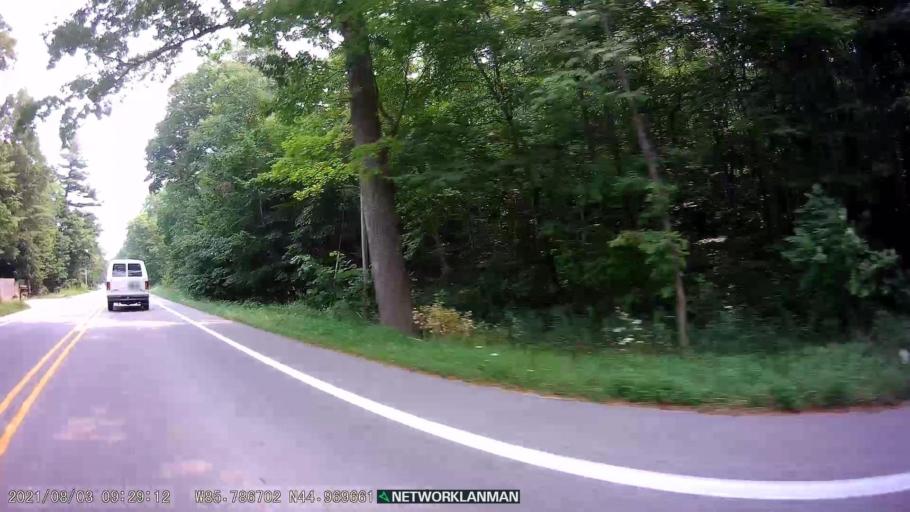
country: US
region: Michigan
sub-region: Leelanau County
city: Leland
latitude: 44.9699
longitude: -85.7865
